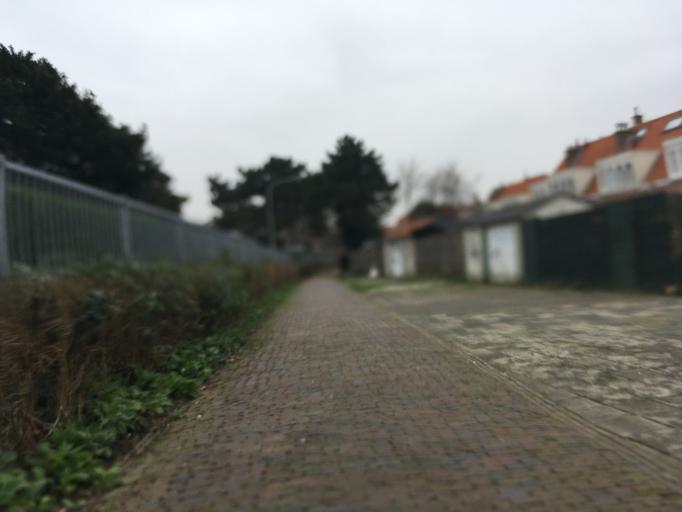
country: NL
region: North Holland
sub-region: Gemeente Haarlem
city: Haarlem
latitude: 52.3996
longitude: 4.6417
